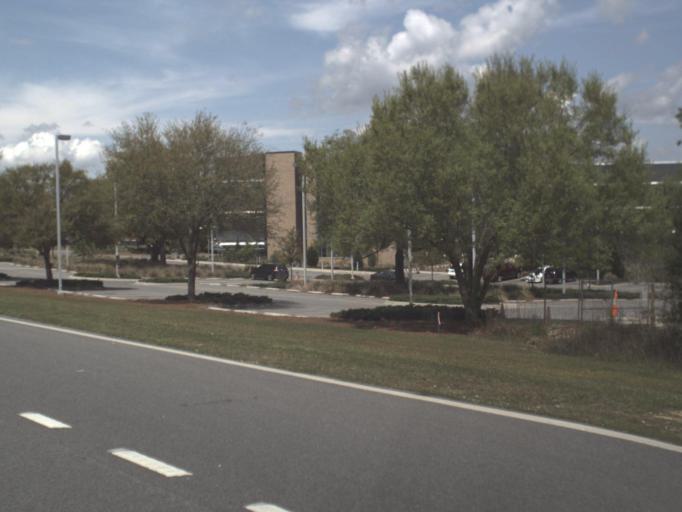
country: US
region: Florida
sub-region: Escambia County
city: Cantonment
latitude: 30.5351
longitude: -87.3530
